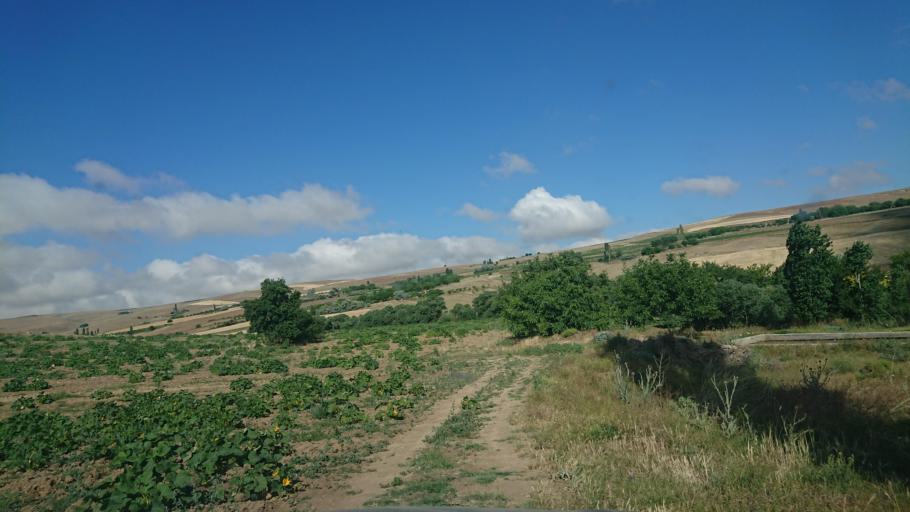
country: TR
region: Aksaray
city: Agacoren
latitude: 38.8460
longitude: 33.9301
